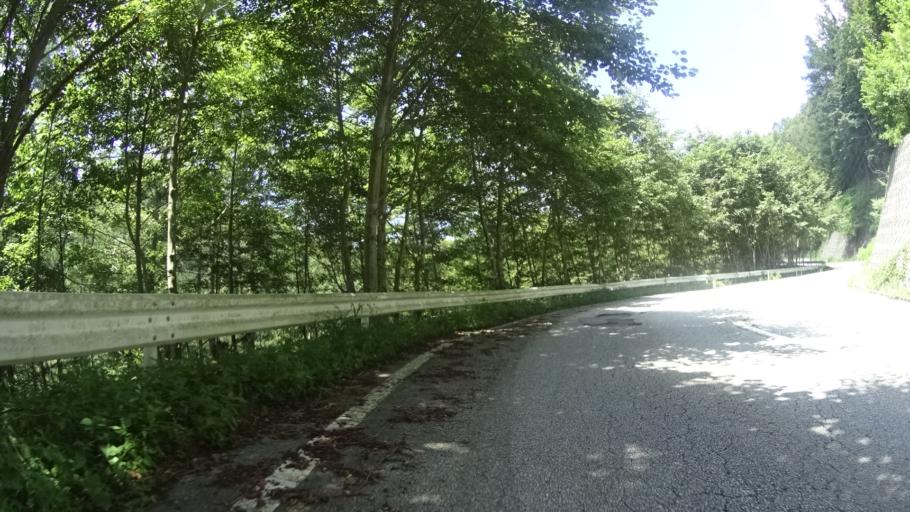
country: JP
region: Yamanashi
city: Enzan
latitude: 35.8043
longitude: 138.6662
